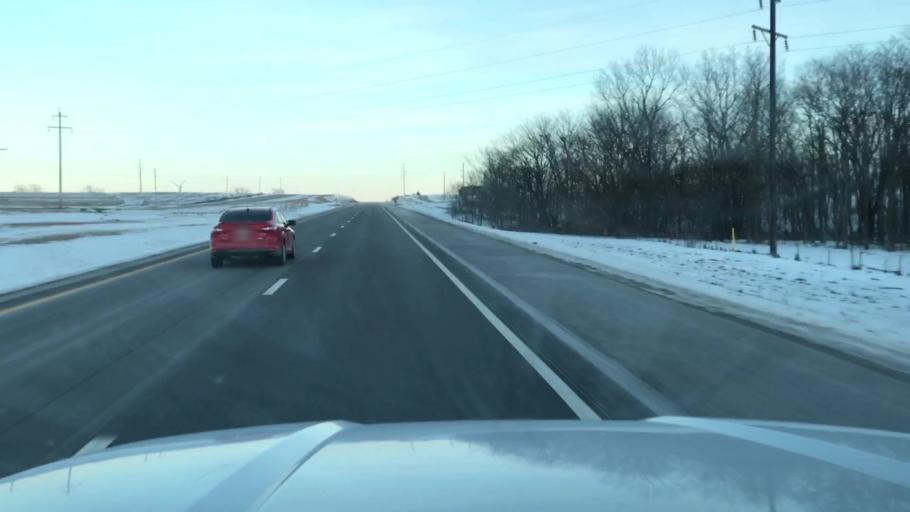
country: US
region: Missouri
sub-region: DeKalb County
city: Maysville
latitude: 39.7619
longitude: -94.4544
